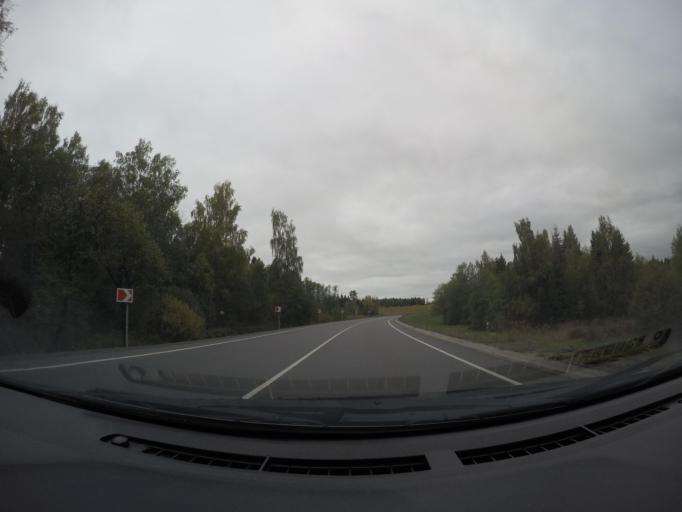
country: RU
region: Moskovskaya
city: Ruza
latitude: 55.7510
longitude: 36.2570
